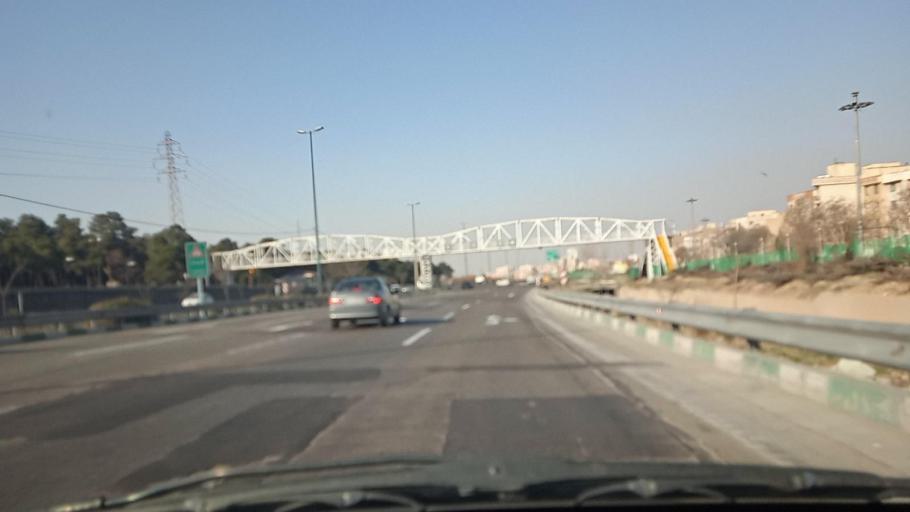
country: IR
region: Tehran
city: Tehran
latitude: 35.7220
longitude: 51.5285
